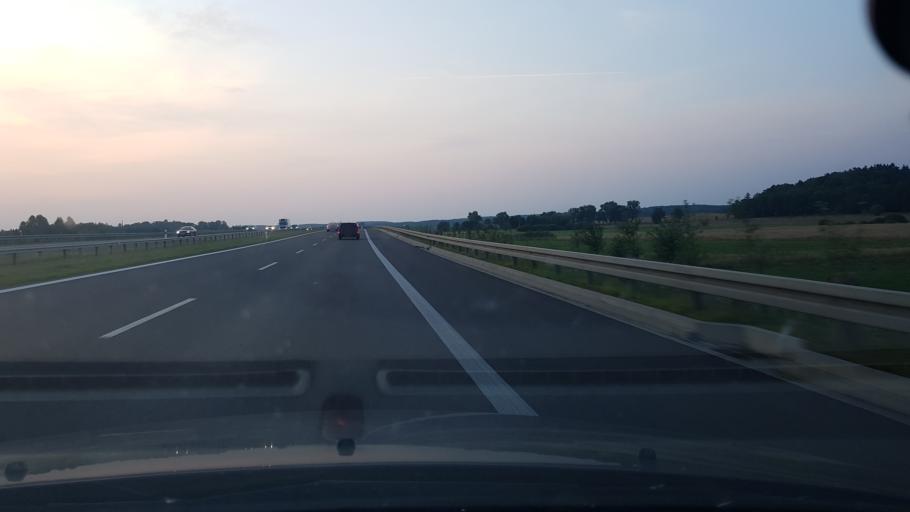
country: PL
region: Warmian-Masurian Voivodeship
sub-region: Powiat nidzicki
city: Nidzica
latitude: 53.3808
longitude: 20.3738
